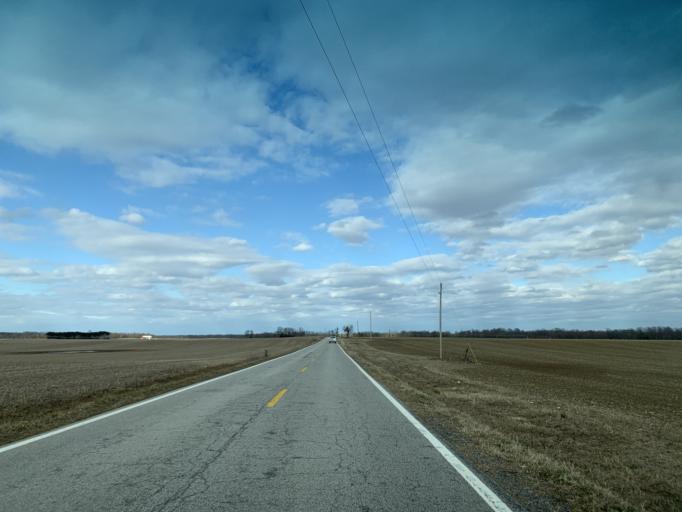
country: US
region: Maryland
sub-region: Caroline County
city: Ridgely
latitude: 38.9801
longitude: -75.9533
